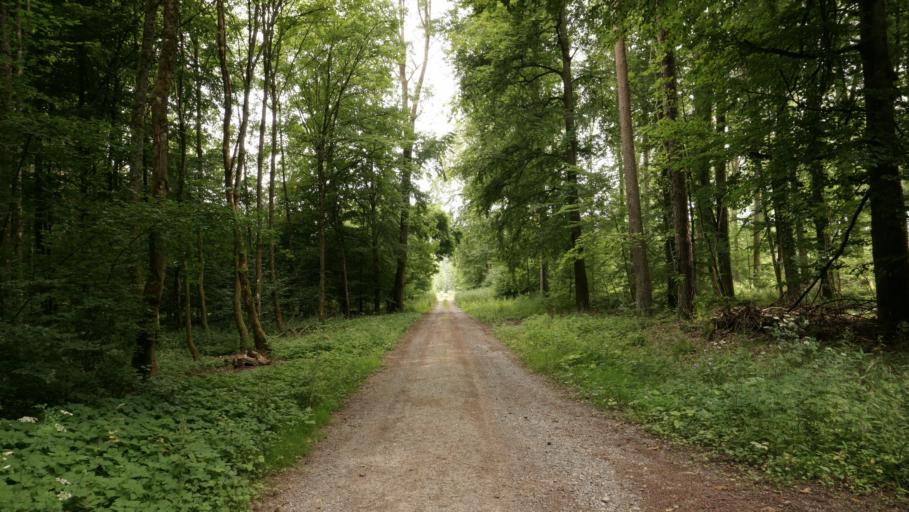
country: DE
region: Baden-Wuerttemberg
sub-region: Karlsruhe Region
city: Mosbach
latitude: 49.3290
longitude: 9.1733
